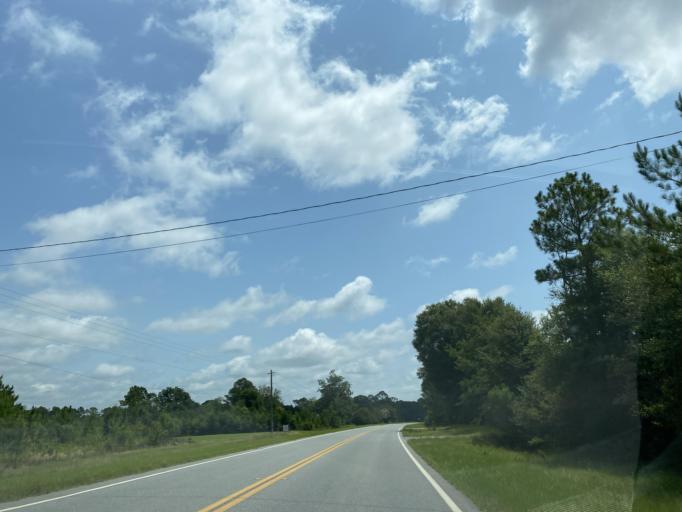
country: US
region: Georgia
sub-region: Telfair County
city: Helena
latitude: 32.0294
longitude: -83.0288
